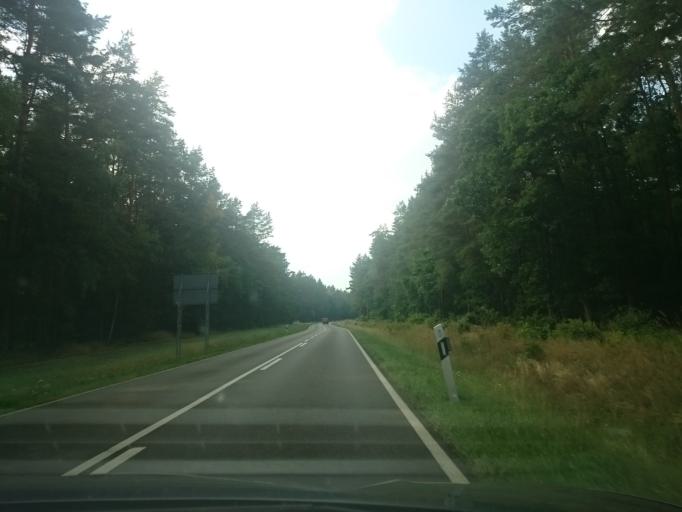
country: DE
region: Mecklenburg-Vorpommern
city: Jatznick
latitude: 53.6377
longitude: 13.9519
